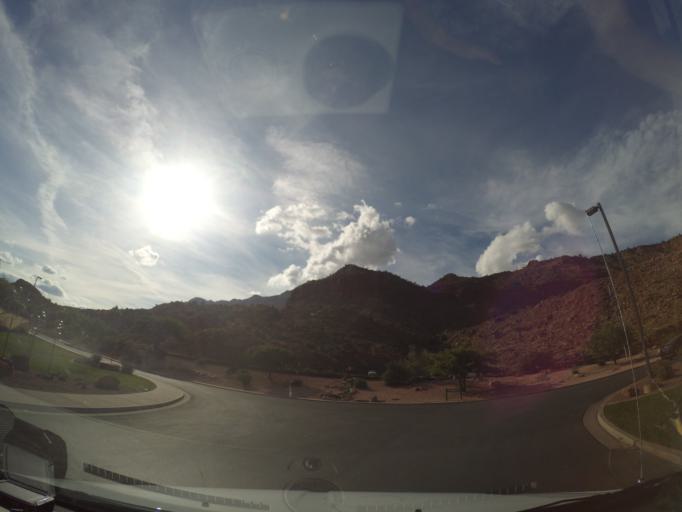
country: US
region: Utah
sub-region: Washington County
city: Hildale
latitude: 37.1993
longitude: -112.9895
